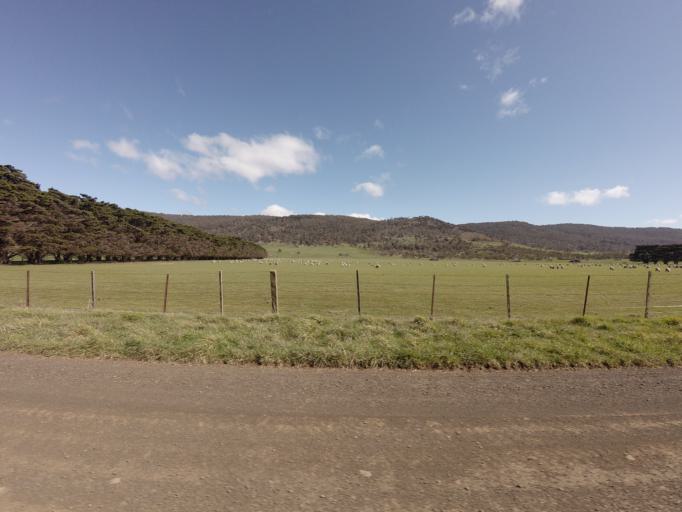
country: AU
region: Tasmania
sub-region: Northern Midlands
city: Evandale
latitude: -41.9569
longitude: 147.4367
